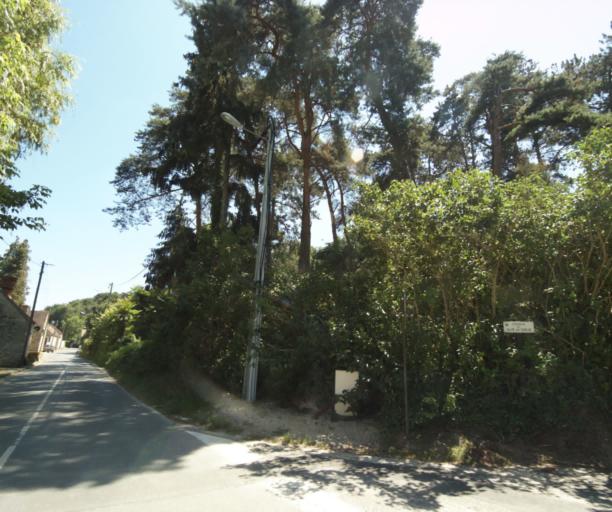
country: FR
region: Ile-de-France
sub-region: Departement de Seine-et-Marne
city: Noisy-sur-Ecole
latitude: 48.3705
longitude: 2.4987
